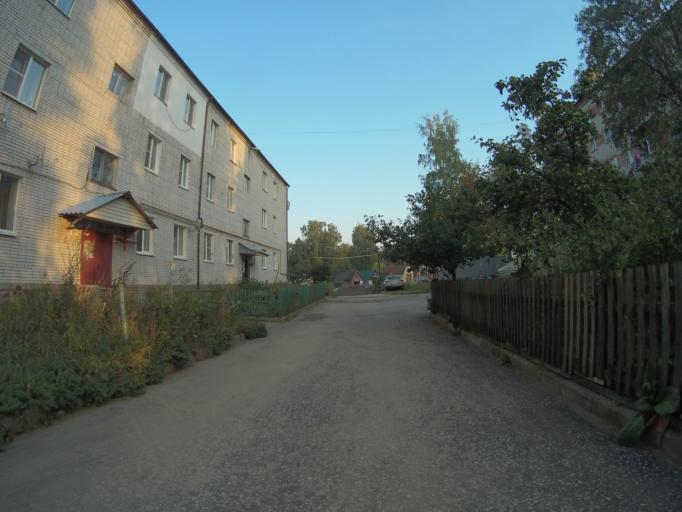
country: RU
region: Vladimir
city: Orgtrud
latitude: 56.1867
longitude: 40.6078
